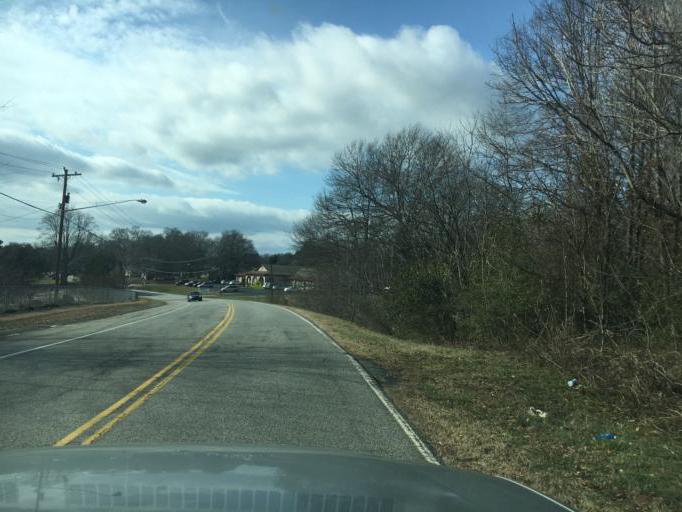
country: US
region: South Carolina
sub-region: Spartanburg County
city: Inman
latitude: 35.0525
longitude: -82.0931
